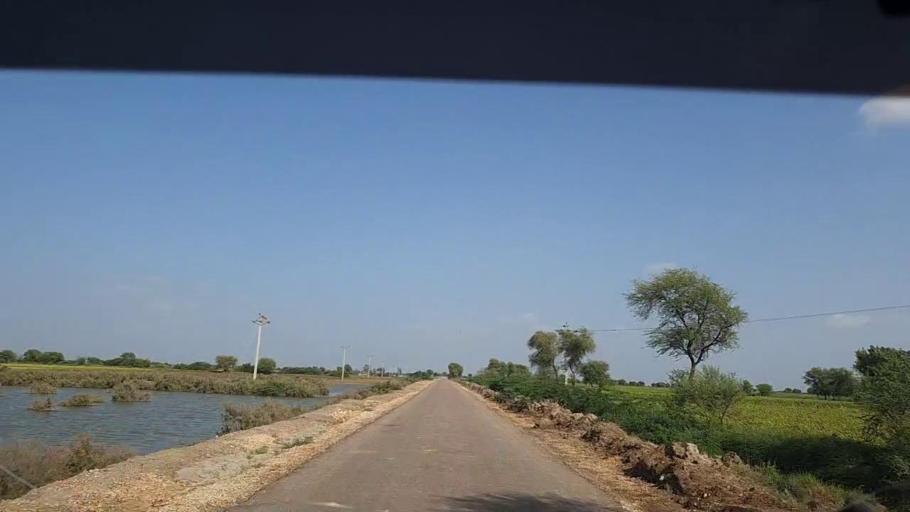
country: PK
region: Sindh
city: Kadhan
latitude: 24.4650
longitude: 68.8394
